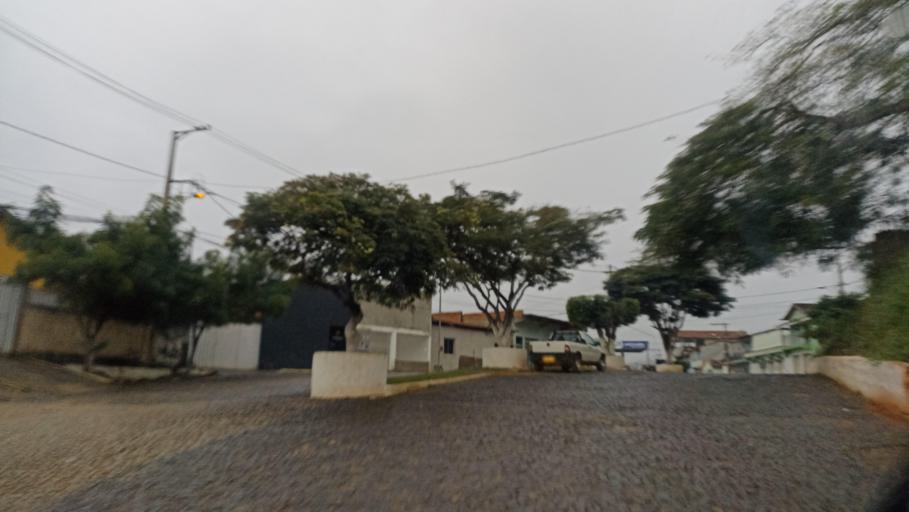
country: BR
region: Bahia
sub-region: Itanhem
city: Itanhem
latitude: -16.7361
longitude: -40.4232
